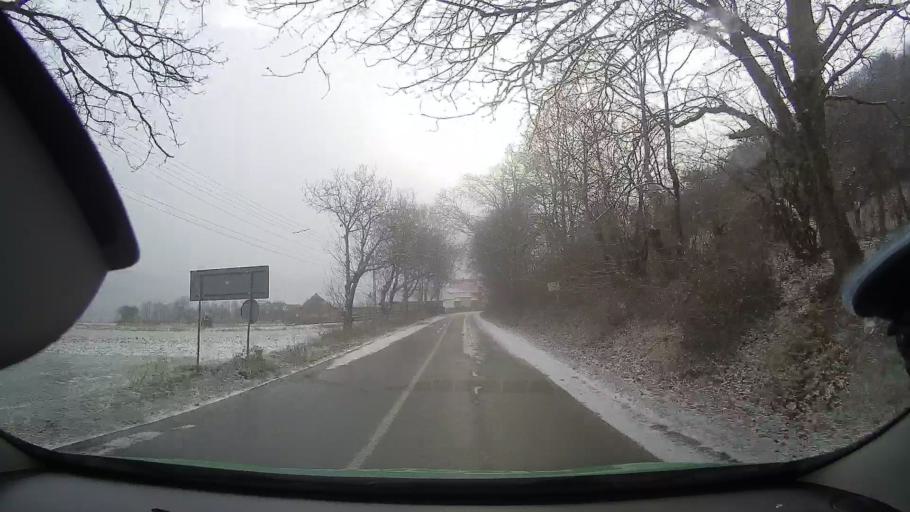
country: RO
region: Alba
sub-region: Comuna Rimetea
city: Rimetea
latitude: 46.4270
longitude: 23.5614
